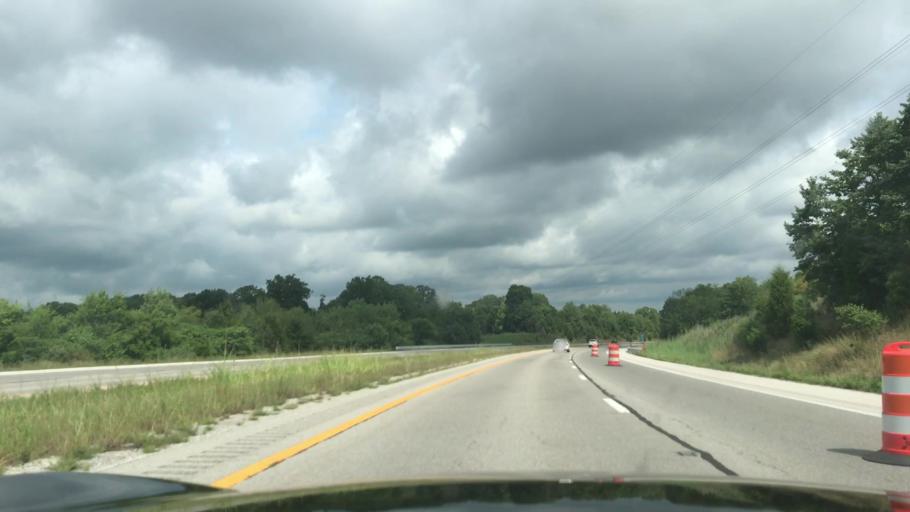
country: US
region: Kentucky
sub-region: Butler County
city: Morgantown
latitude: 37.0996
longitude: -86.6368
